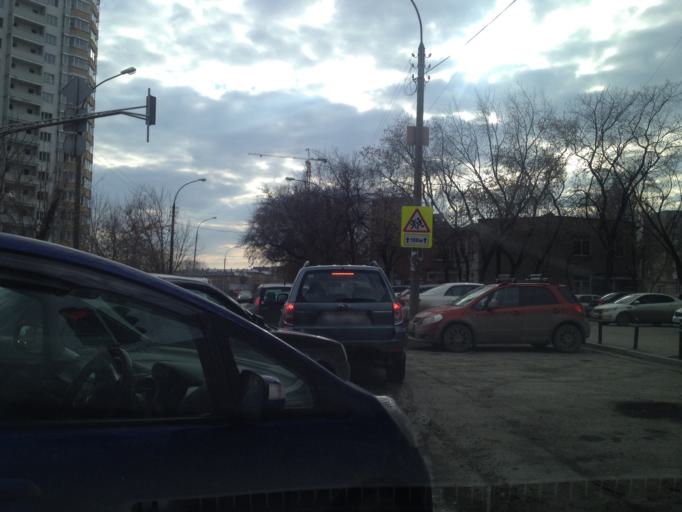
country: RU
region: Sverdlovsk
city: Yekaterinburg
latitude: 56.8537
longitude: 60.5820
